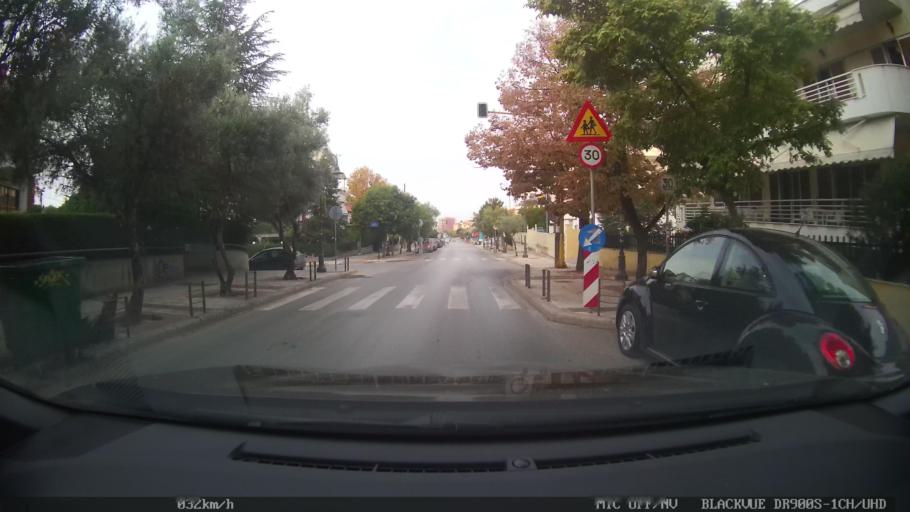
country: GR
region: Central Macedonia
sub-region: Nomos Thessalonikis
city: Pylaia
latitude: 40.5977
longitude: 22.9832
